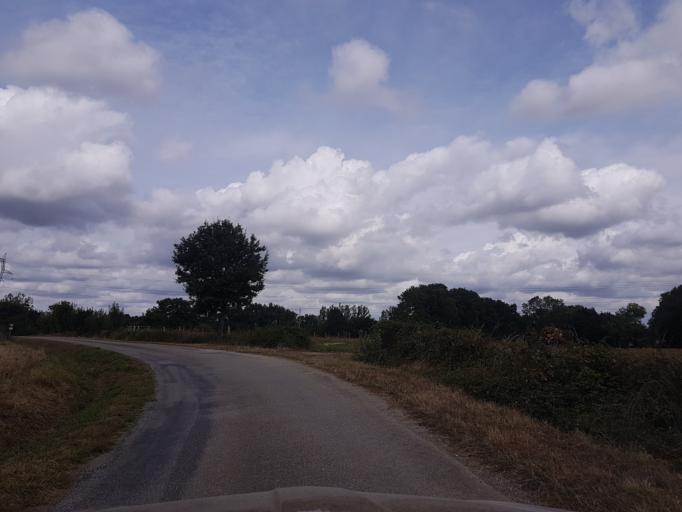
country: FR
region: Pays de la Loire
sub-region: Departement de la Loire-Atlantique
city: Petit-Mars
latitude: 47.4205
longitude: -1.4472
